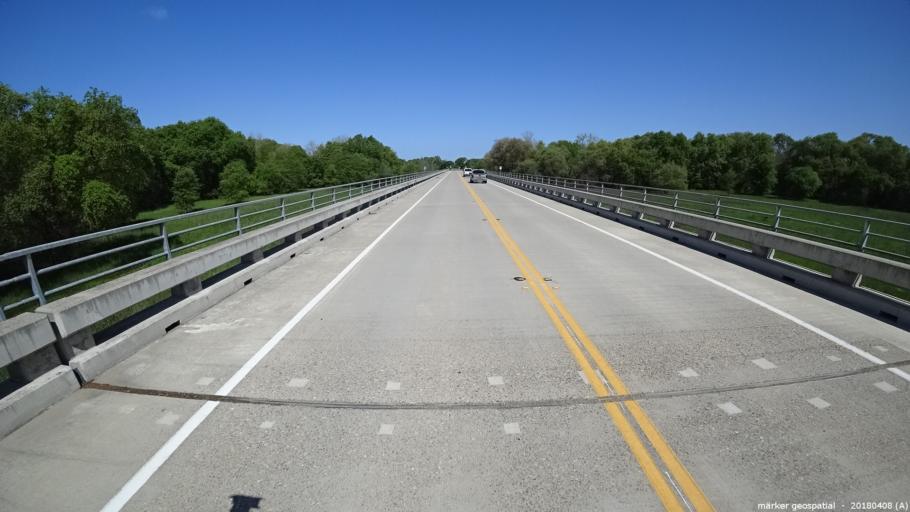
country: US
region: California
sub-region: San Joaquin County
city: Thornton
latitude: 38.2587
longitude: -121.4399
